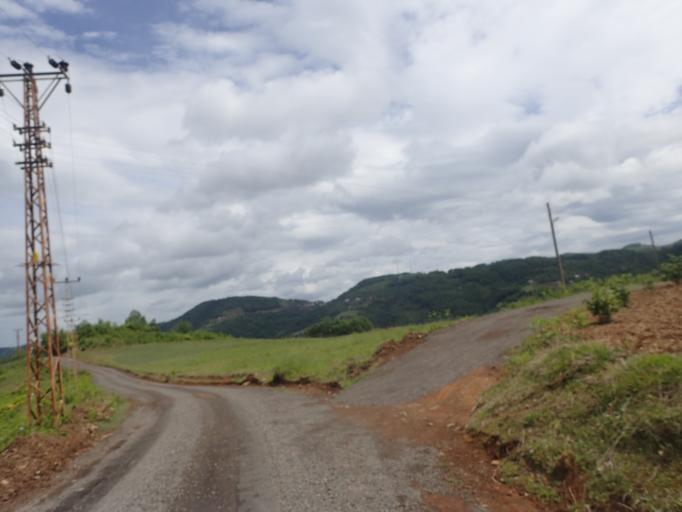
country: TR
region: Ordu
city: Akkus
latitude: 40.9109
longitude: 36.8866
